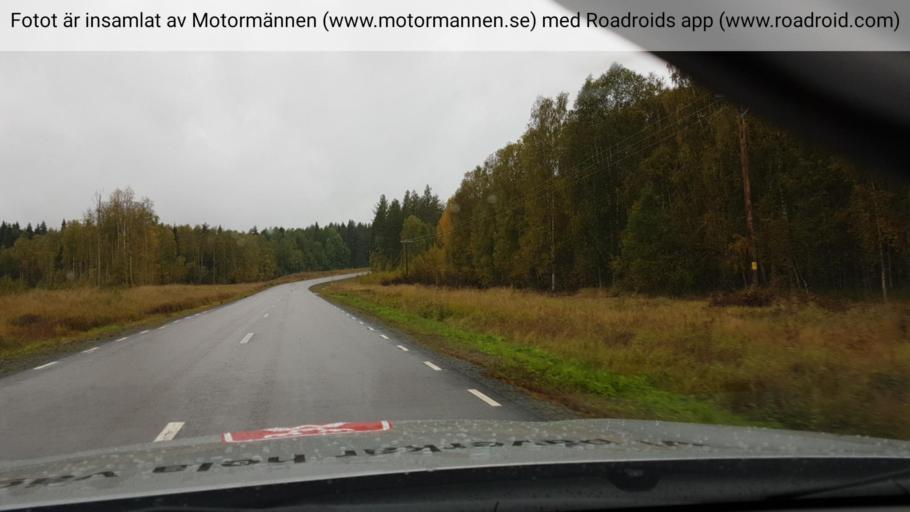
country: SE
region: Norrbotten
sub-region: Lulea Kommun
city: Sodra Sunderbyn
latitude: 65.8215
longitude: 21.9185
